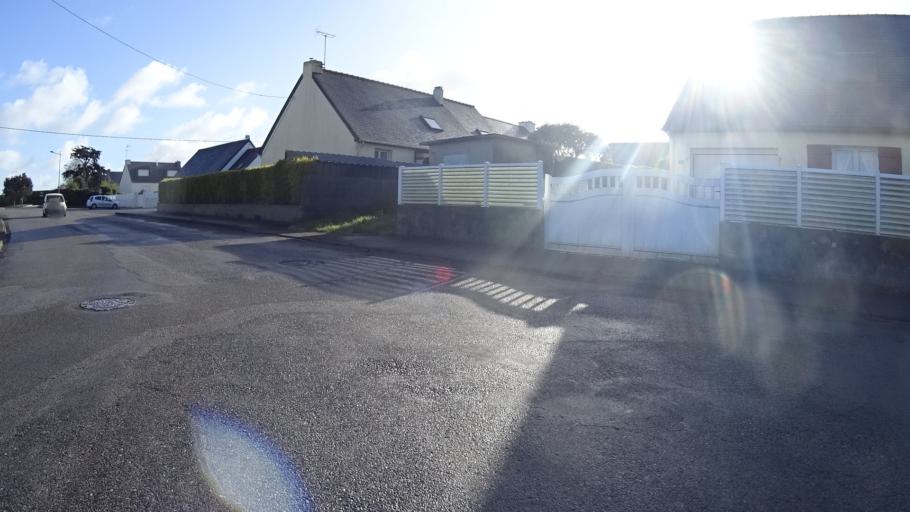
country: FR
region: Brittany
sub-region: Departement du Finistere
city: Plouarzel
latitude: 48.4326
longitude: -4.7214
